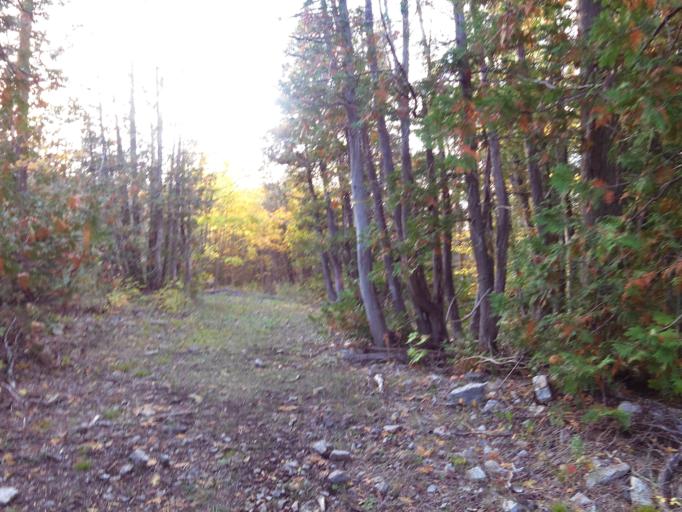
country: CA
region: Ontario
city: Pembroke
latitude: 45.5351
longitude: -77.0932
